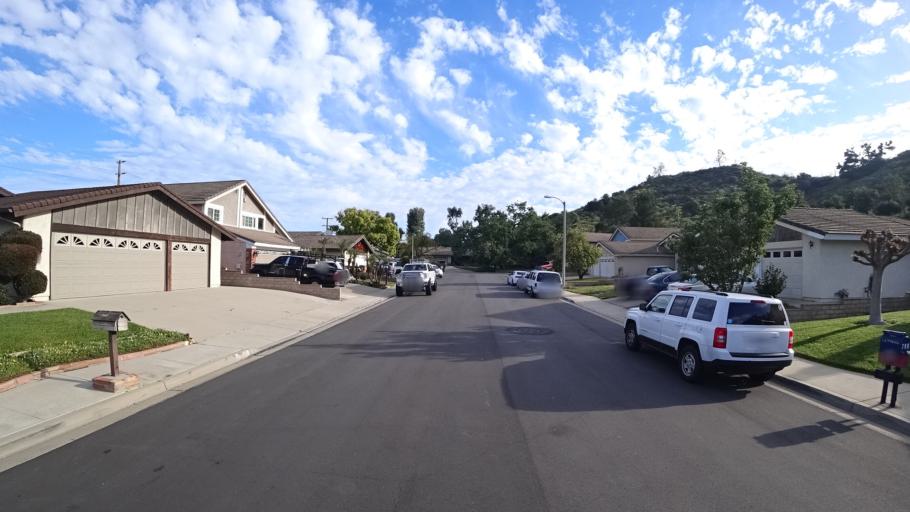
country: US
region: California
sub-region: Ventura County
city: Casa Conejo
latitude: 34.1644
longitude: -118.9558
